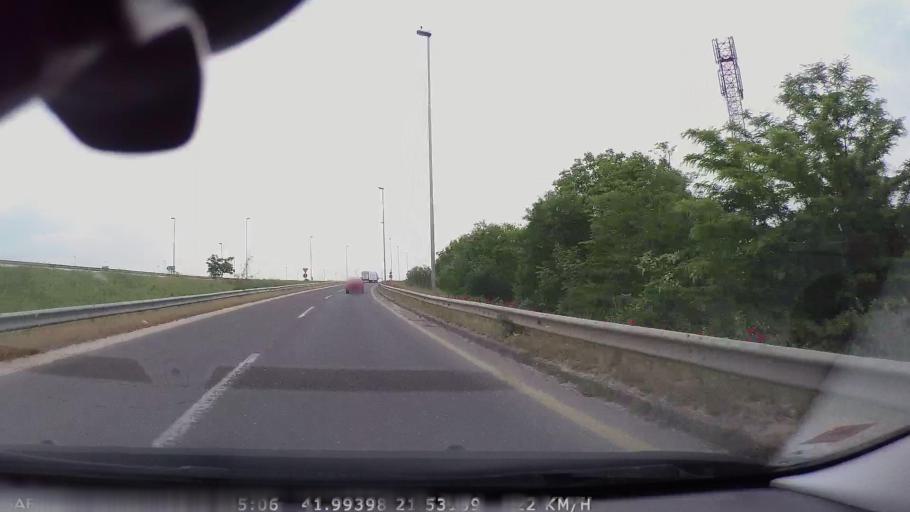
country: MK
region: Ilinden
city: Jurumleri
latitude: 41.9934
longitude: 21.5327
